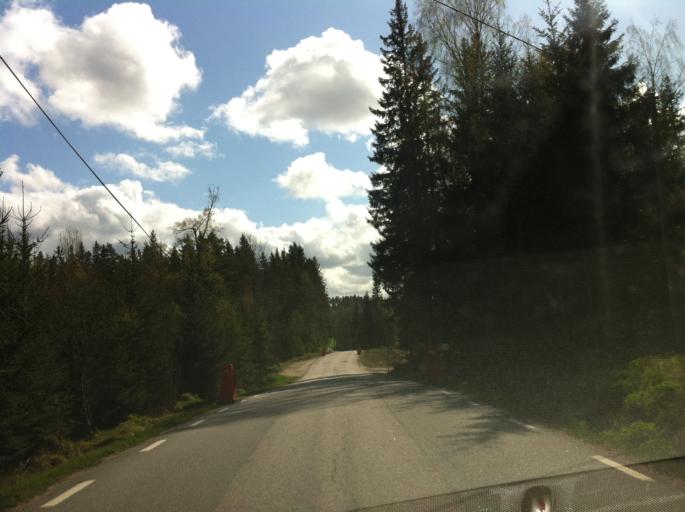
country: SE
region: Vaestra Goetaland
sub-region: Alingsas Kommun
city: Alingsas
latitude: 57.8309
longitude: 12.6480
